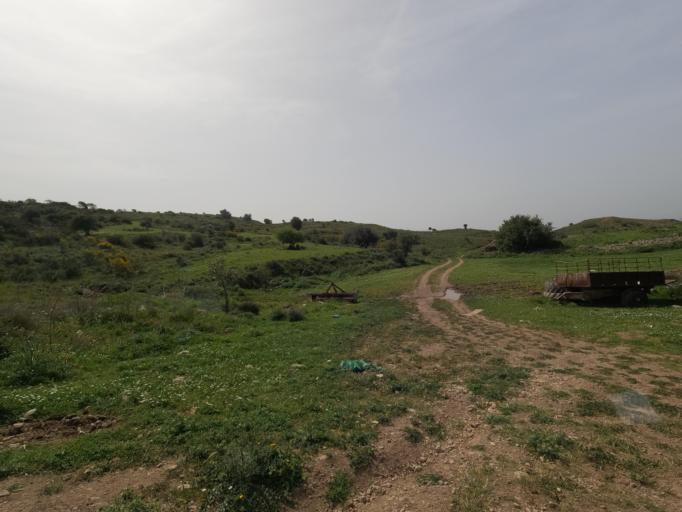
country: CY
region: Pafos
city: Pegeia
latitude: 34.9746
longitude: 32.3409
